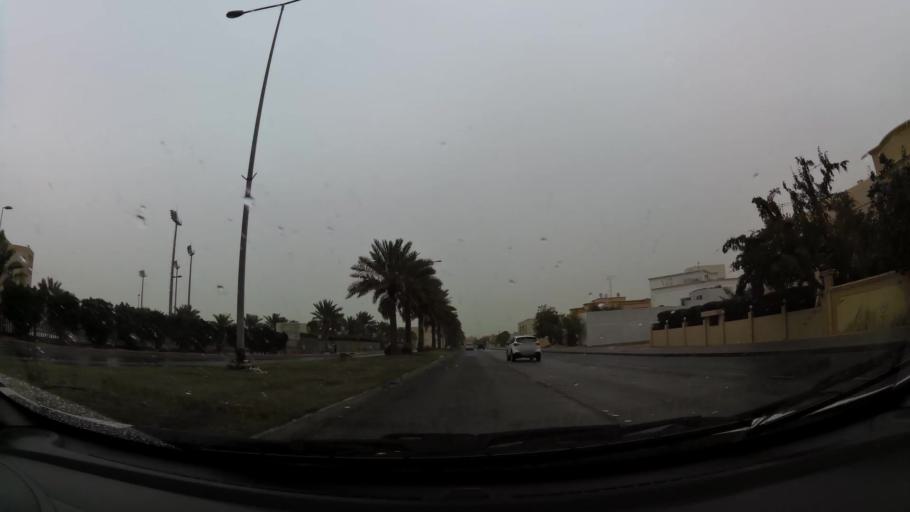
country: BH
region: Northern
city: Madinat `Isa
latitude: 26.1735
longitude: 50.5498
